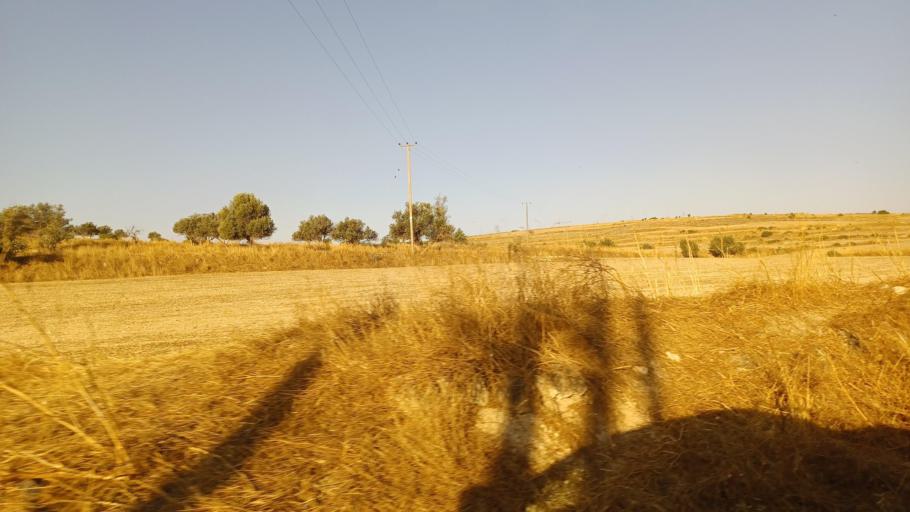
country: CY
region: Larnaka
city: Athienou
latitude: 35.0467
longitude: 33.5154
